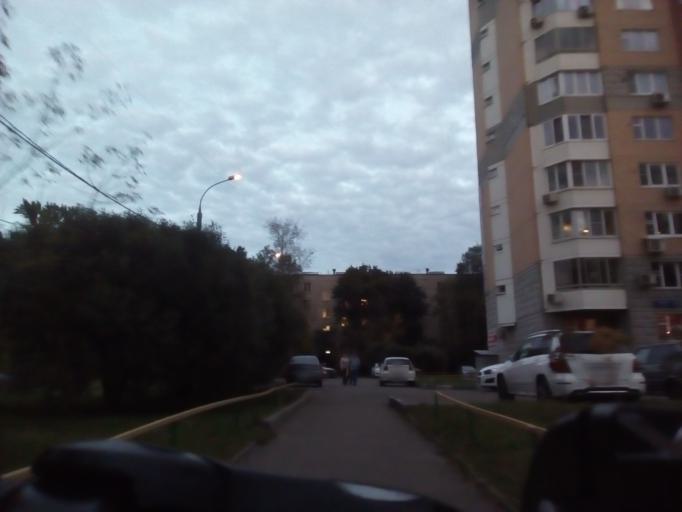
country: RU
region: Moscow
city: Leonovo
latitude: 55.8552
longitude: 37.6488
